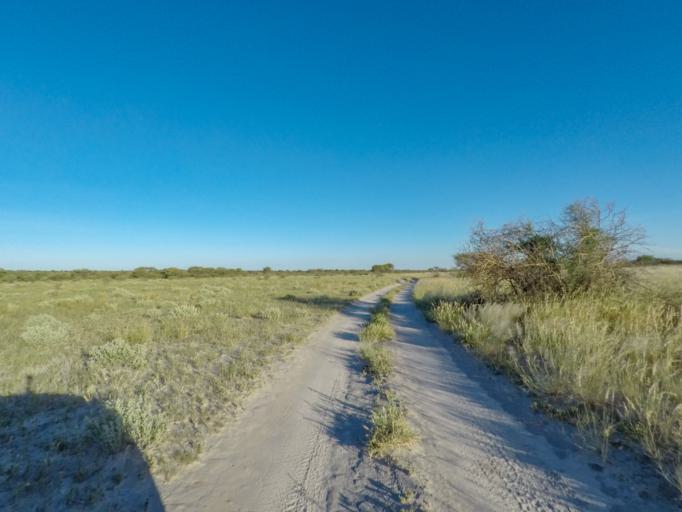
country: BW
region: Central
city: Rakops
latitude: -21.3808
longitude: 23.7932
